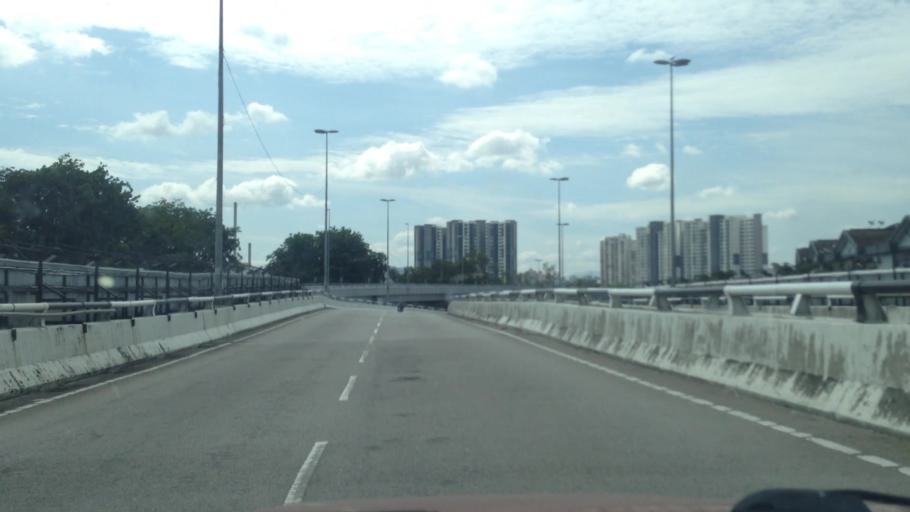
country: MY
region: Kuala Lumpur
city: Kuala Lumpur
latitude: 3.0919
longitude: 101.6893
